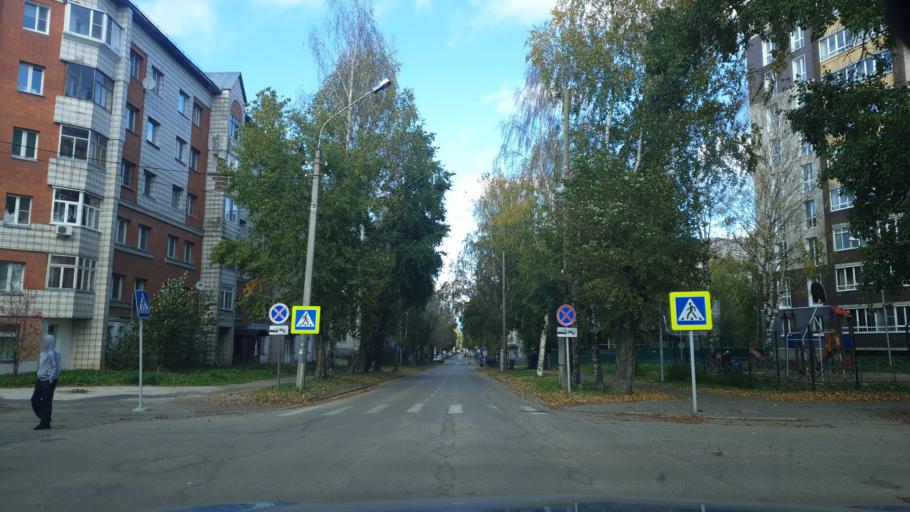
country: RU
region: Komi Republic
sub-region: Syktyvdinskiy Rayon
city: Syktyvkar
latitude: 61.6623
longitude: 50.8422
